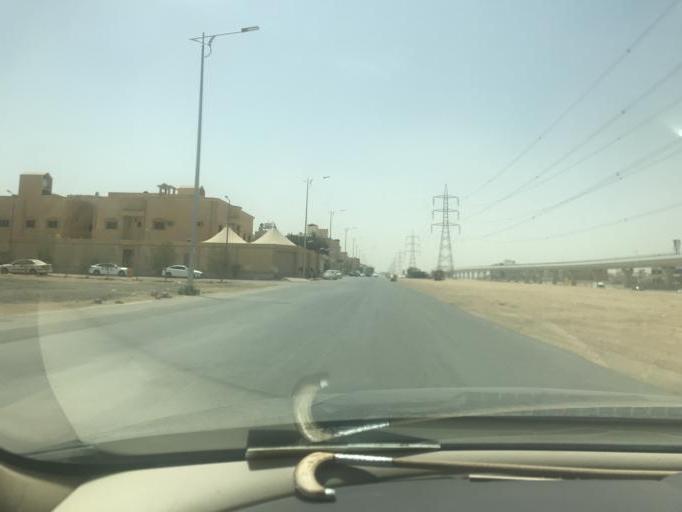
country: SA
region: Ar Riyad
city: Riyadh
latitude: 24.7995
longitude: 46.6942
